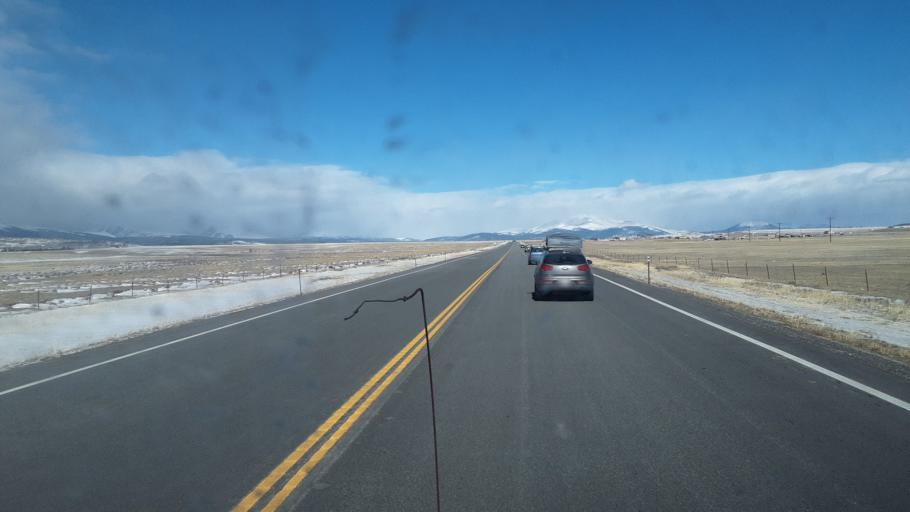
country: US
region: Colorado
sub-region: Park County
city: Fairplay
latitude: 39.1071
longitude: -105.9904
